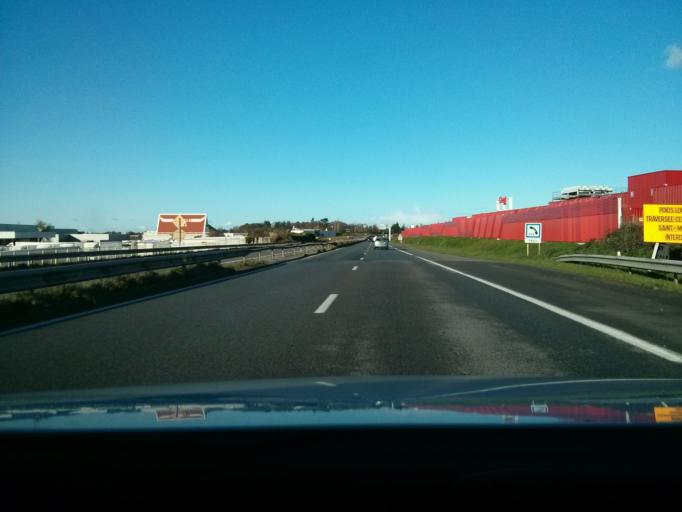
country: FR
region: Brittany
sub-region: Departement du Finistere
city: Morlaix
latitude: 48.5714
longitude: -3.8539
